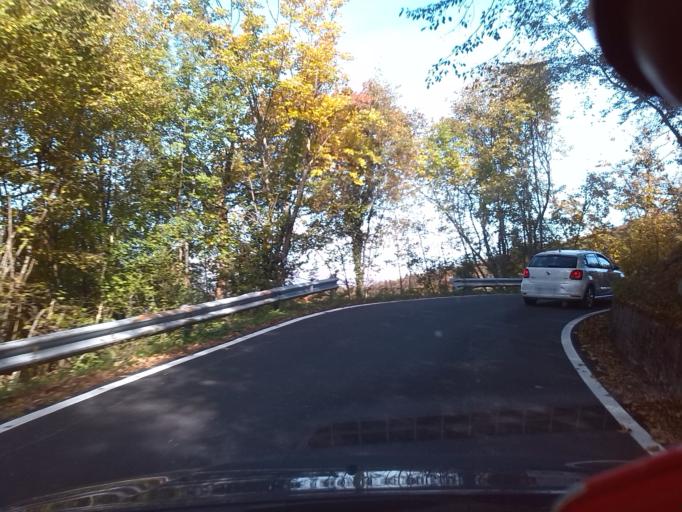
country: IT
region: Friuli Venezia Giulia
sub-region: Provincia di Udine
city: San Leonardo
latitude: 46.0962
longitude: 13.5221
